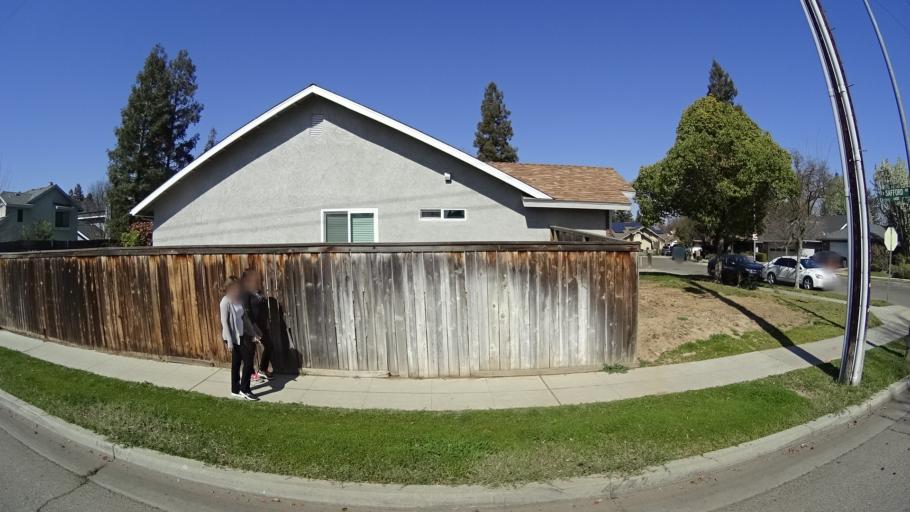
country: US
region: California
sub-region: Fresno County
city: Fresno
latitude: 36.8301
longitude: -119.8110
